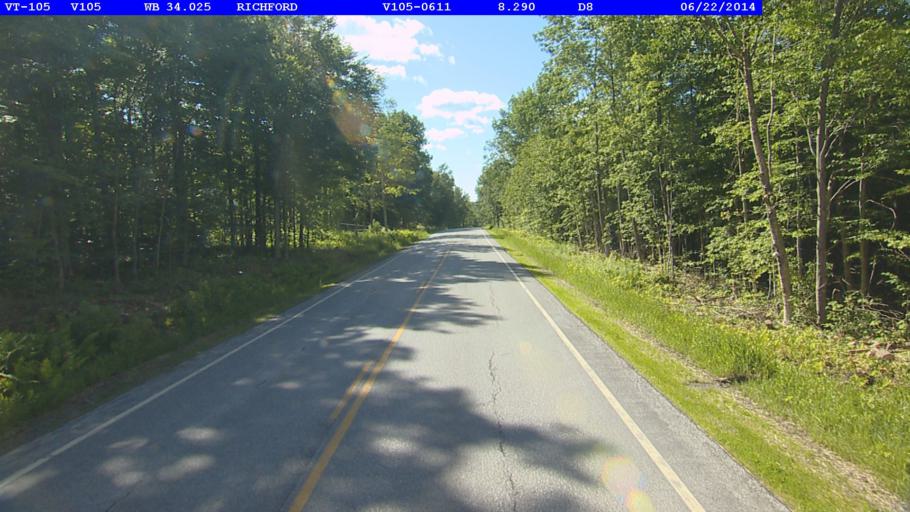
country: US
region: Vermont
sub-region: Franklin County
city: Richford
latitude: 44.9928
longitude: -72.5658
